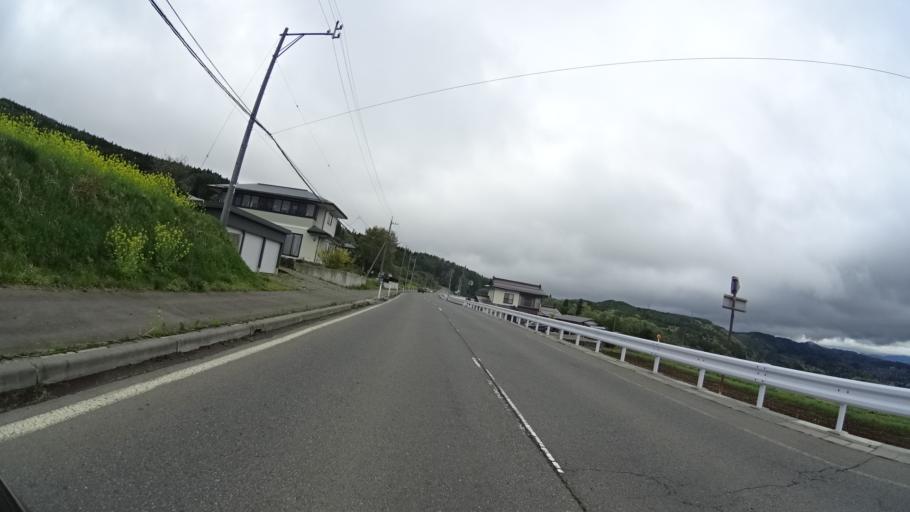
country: JP
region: Nagano
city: Nagano-shi
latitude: 36.7438
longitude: 138.2054
